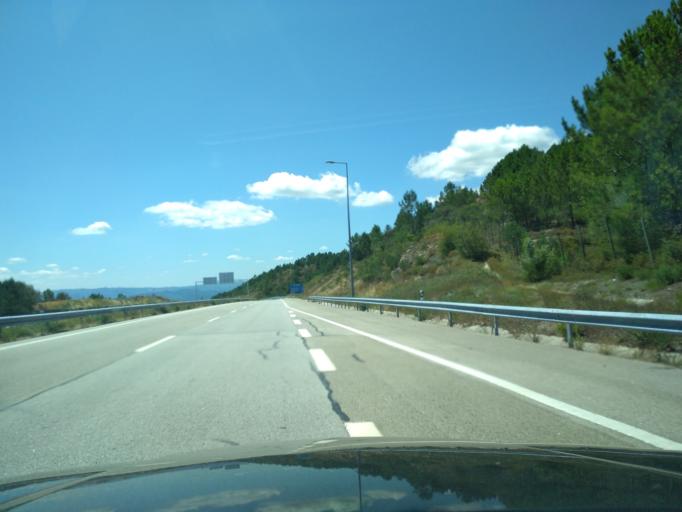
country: PT
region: Vila Real
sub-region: Ribeira de Pena
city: Ribeira de Pena
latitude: 41.4965
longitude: -7.8068
